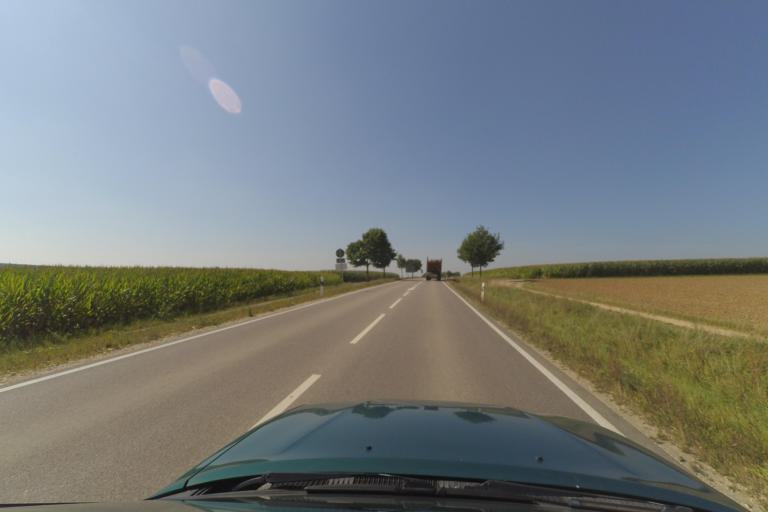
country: DE
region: Bavaria
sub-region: Swabia
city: Bachhagel
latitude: 48.6282
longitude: 10.3464
